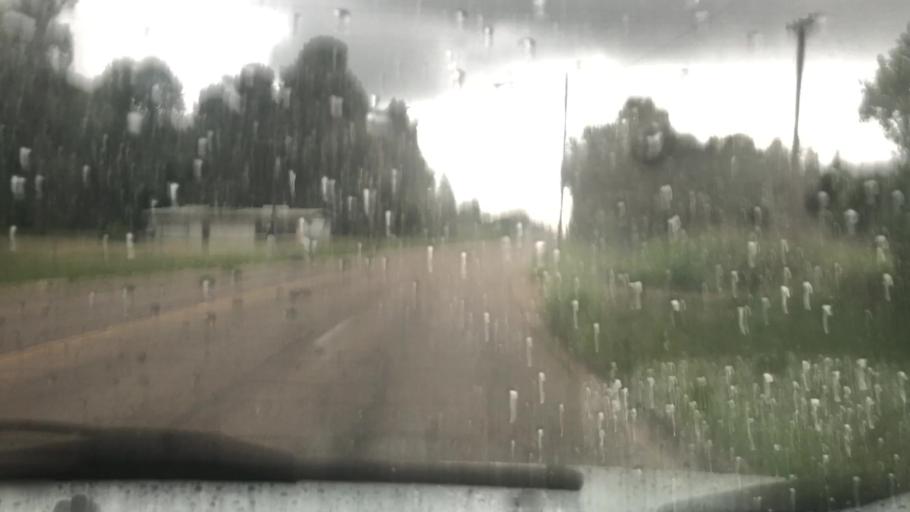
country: US
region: Texas
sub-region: Bowie County
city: Wake Village
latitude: 33.4091
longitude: -94.0803
